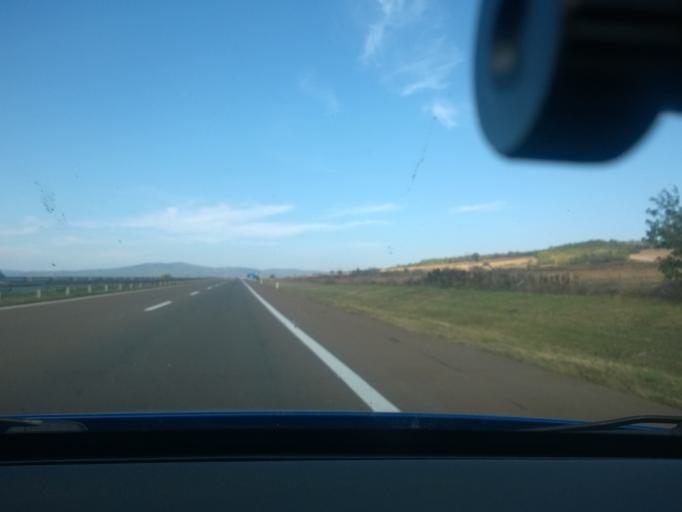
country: RS
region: Central Serbia
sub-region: Nisavski Okrug
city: Razanj
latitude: 43.6109
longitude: 21.6055
